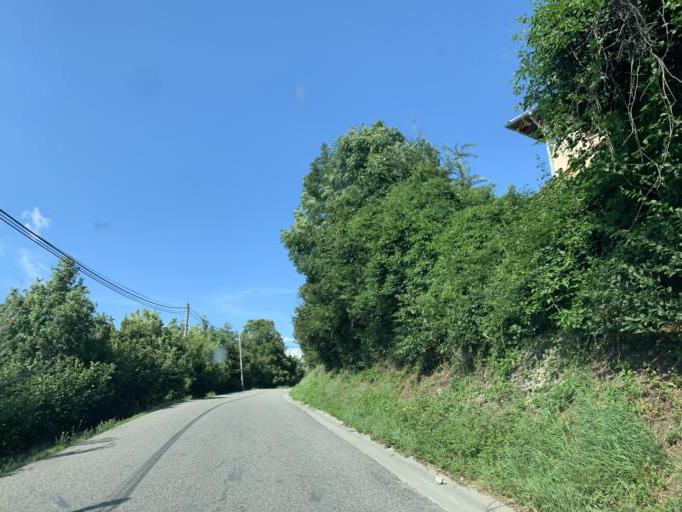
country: FR
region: Provence-Alpes-Cote d'Azur
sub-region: Departement des Hautes-Alpes
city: Embrun
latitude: 44.5868
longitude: 6.5324
